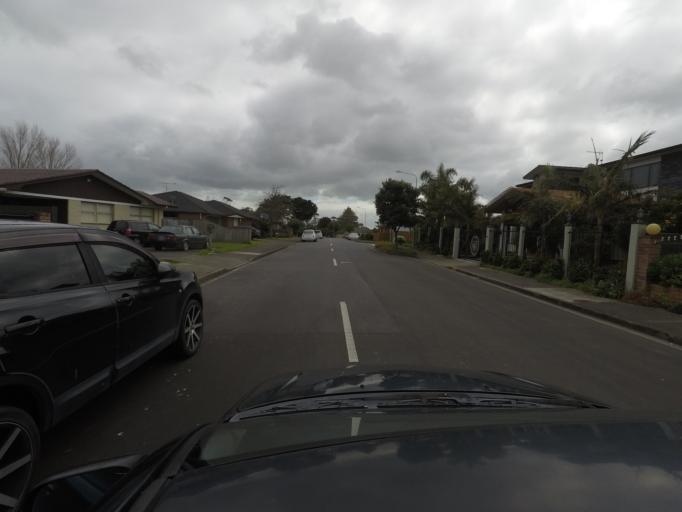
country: NZ
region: Auckland
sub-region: Auckland
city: Tamaki
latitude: -36.9331
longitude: 174.8548
